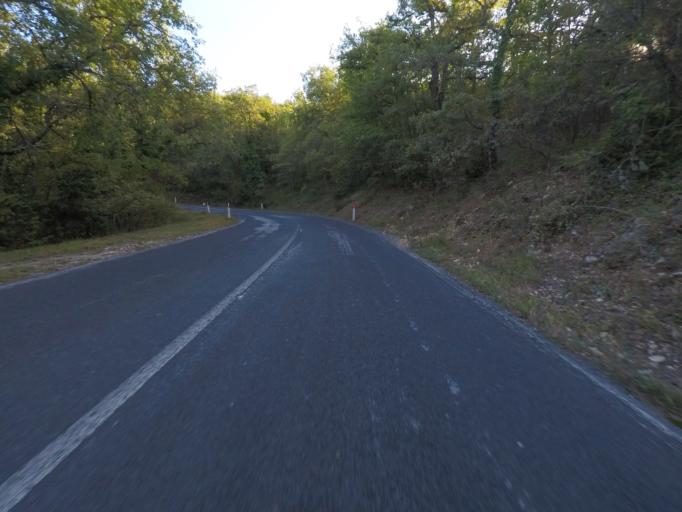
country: IT
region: Tuscany
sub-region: Provincia di Siena
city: Radda in Chianti
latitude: 43.4609
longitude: 11.3853
